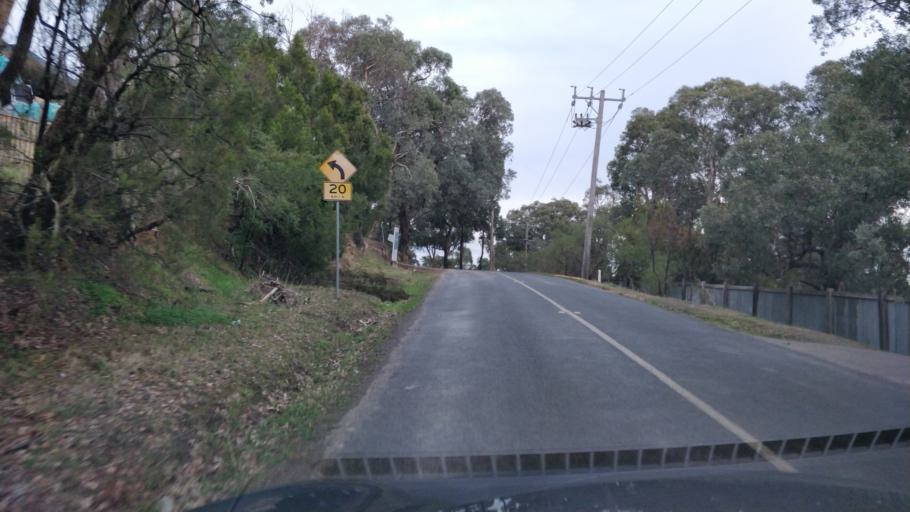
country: AU
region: Victoria
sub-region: Nillumbik
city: Research
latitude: -37.6948
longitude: 145.1800
